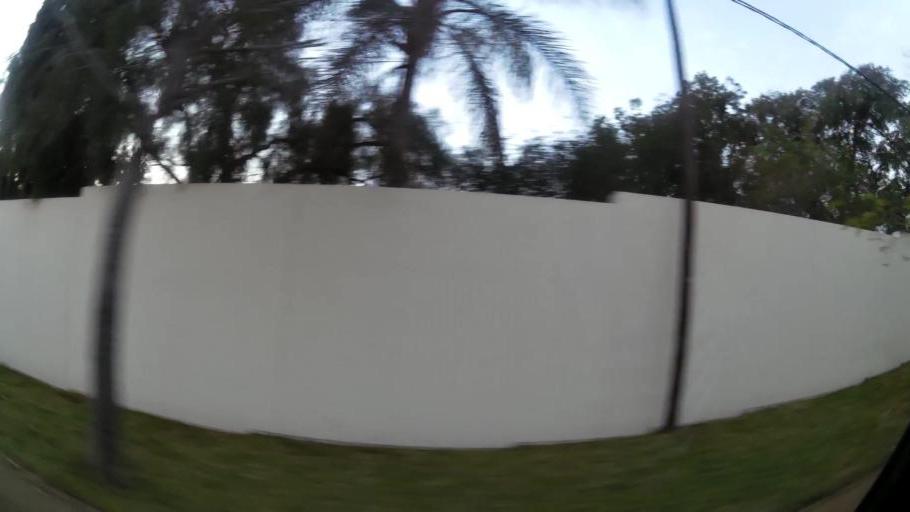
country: ZA
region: Gauteng
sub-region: City of Johannesburg Metropolitan Municipality
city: Midrand
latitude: -25.9803
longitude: 28.0723
